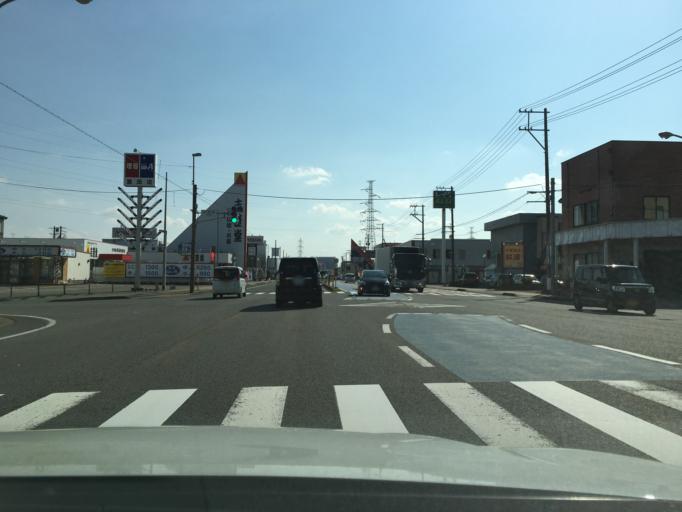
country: JP
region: Yamagata
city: Sakata
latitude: 38.9013
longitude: 139.8562
